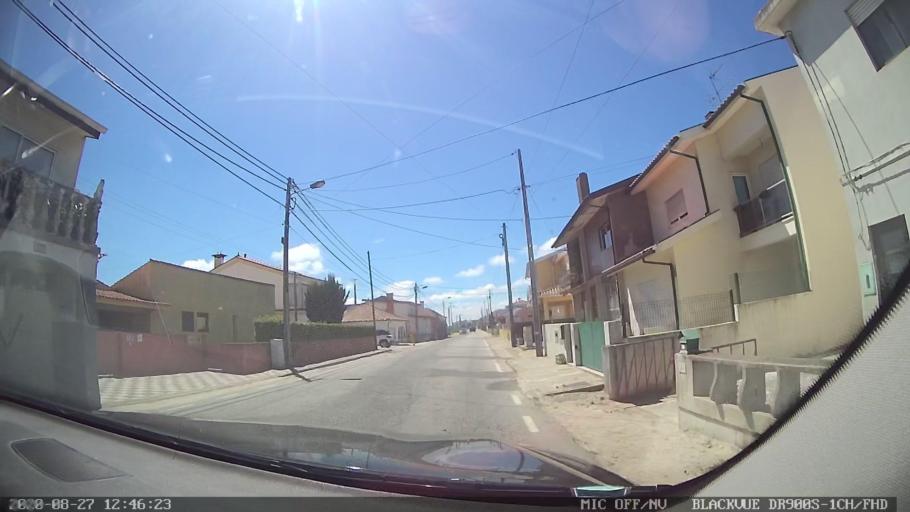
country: PT
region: Aveiro
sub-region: Ilhavo
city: Ilhavo
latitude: 40.6129
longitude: -8.6840
